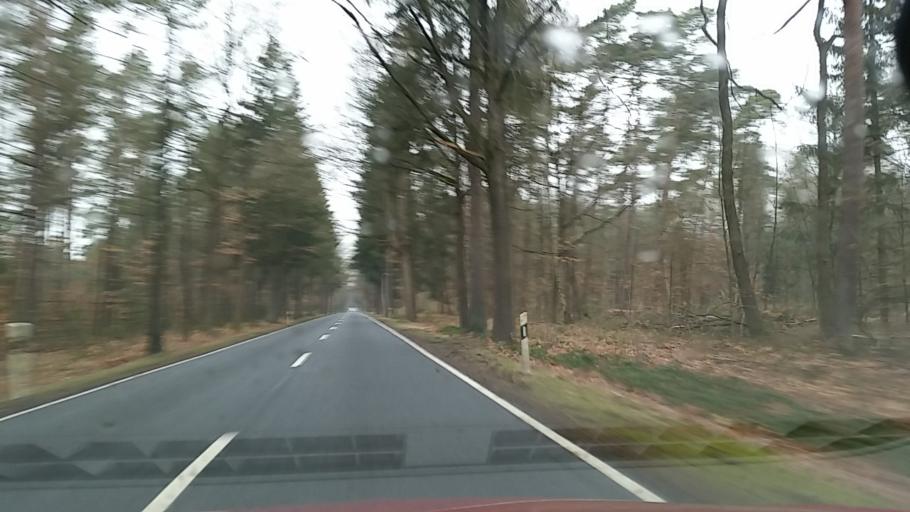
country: DE
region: Lower Saxony
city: Sprakensehl
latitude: 52.7817
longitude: 10.4201
